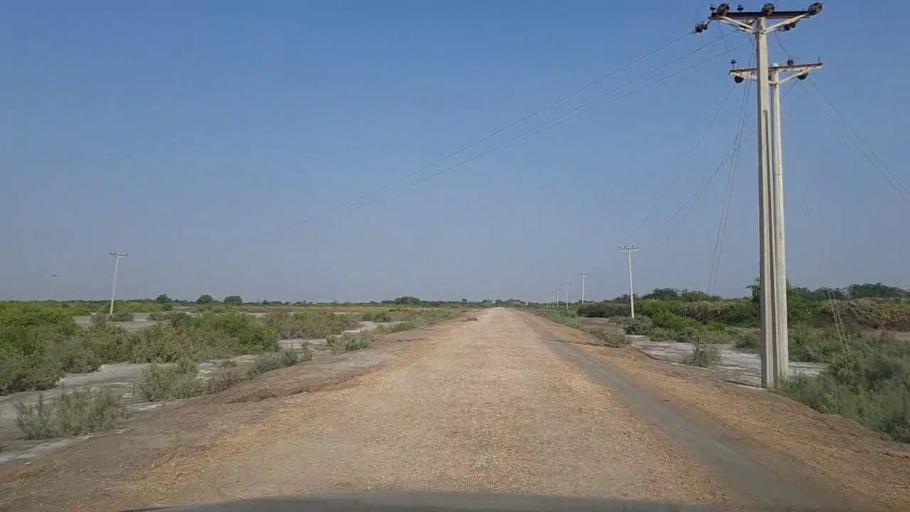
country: PK
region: Sindh
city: Thatta
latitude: 24.6063
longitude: 67.9548
